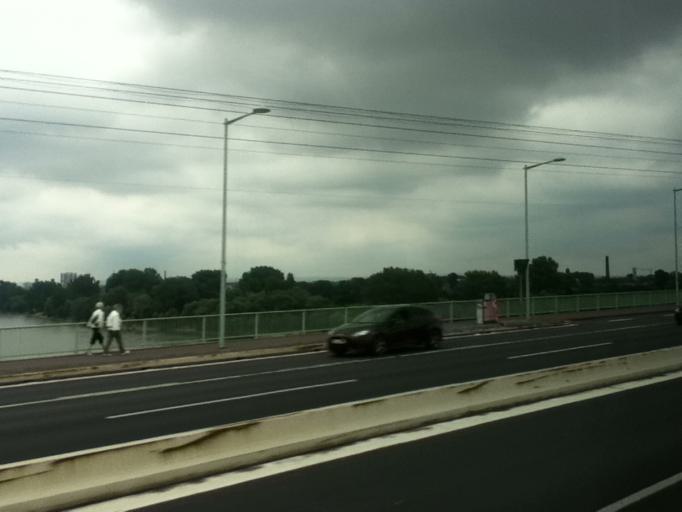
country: DE
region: North Rhine-Westphalia
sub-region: Regierungsbezirk Koln
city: Riehl
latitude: 50.9549
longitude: 6.9749
